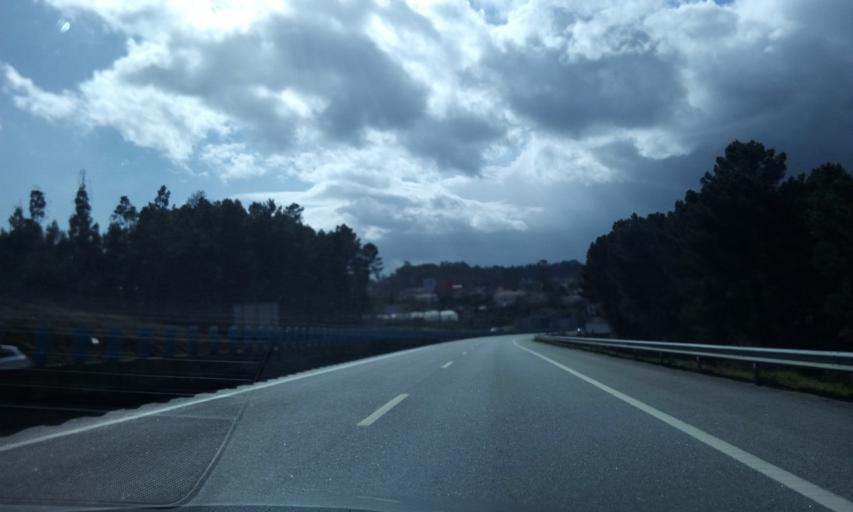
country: PT
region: Viseu
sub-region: Mangualde
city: Mangualde
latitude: 40.6278
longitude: -7.7943
